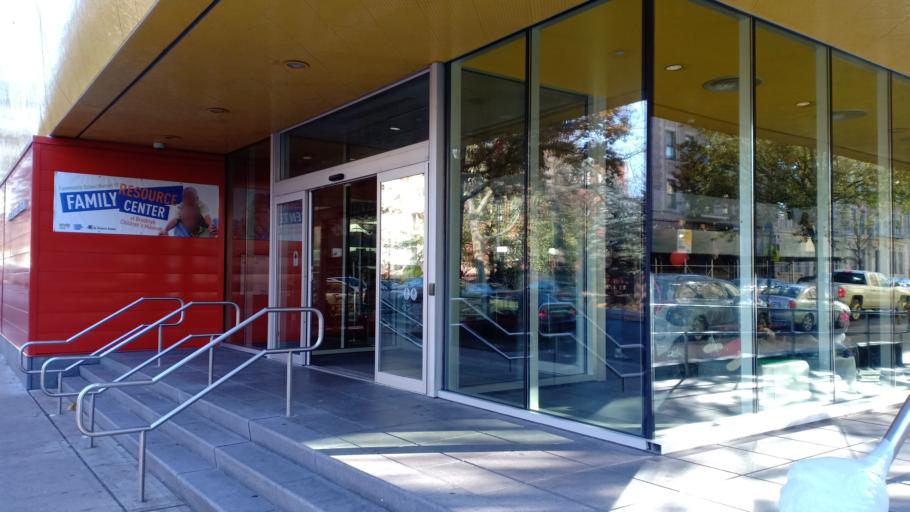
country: US
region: New York
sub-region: Kings County
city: Brooklyn
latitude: 40.6748
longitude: -73.9442
